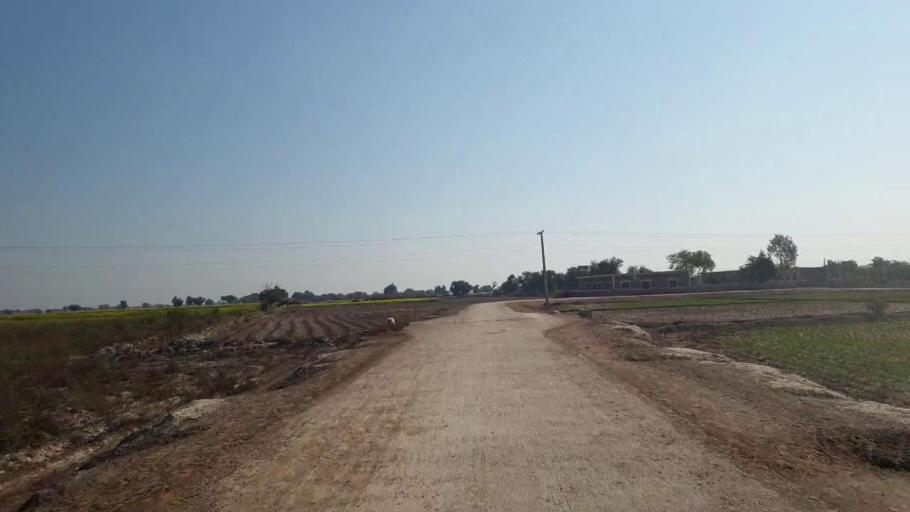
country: PK
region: Sindh
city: Shahpur Chakar
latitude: 26.0817
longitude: 68.6252
